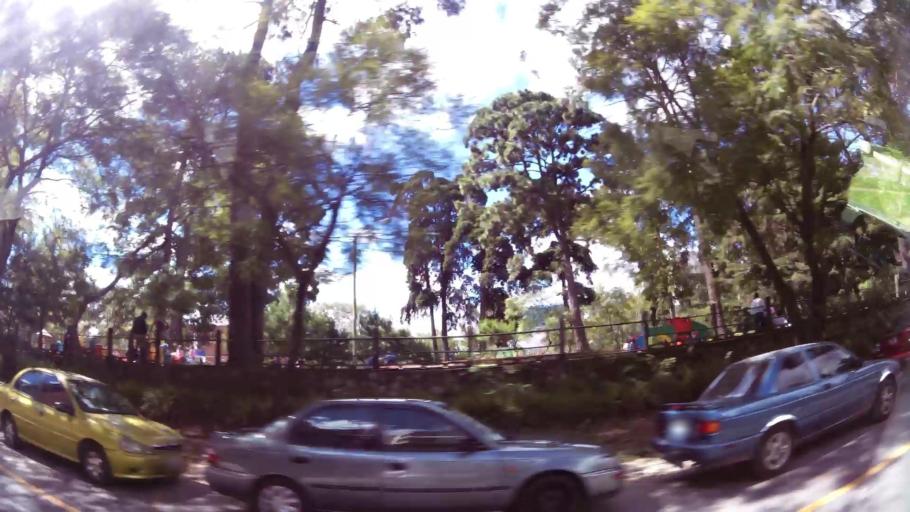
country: GT
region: Guatemala
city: Santa Catarina Pinula
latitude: 14.5903
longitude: -90.5192
